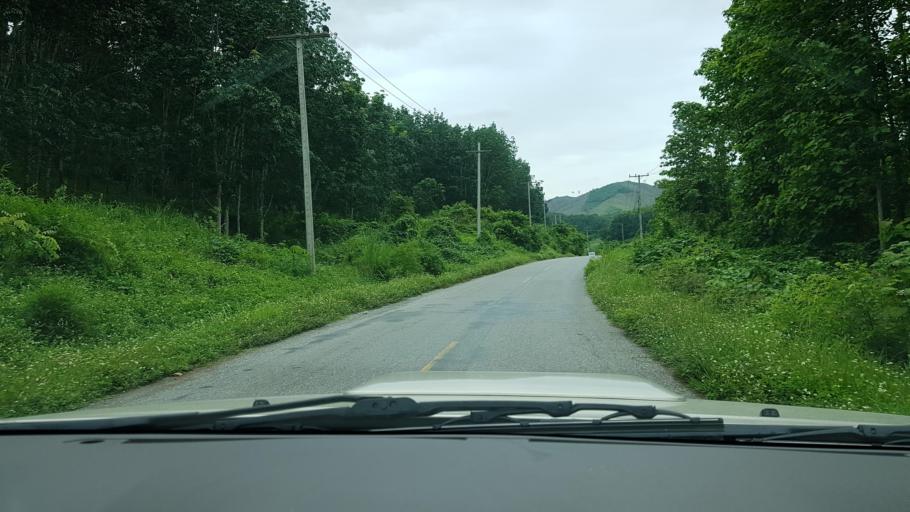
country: LA
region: Loungnamtha
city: Muang Nale
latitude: 20.2000
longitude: 101.5301
